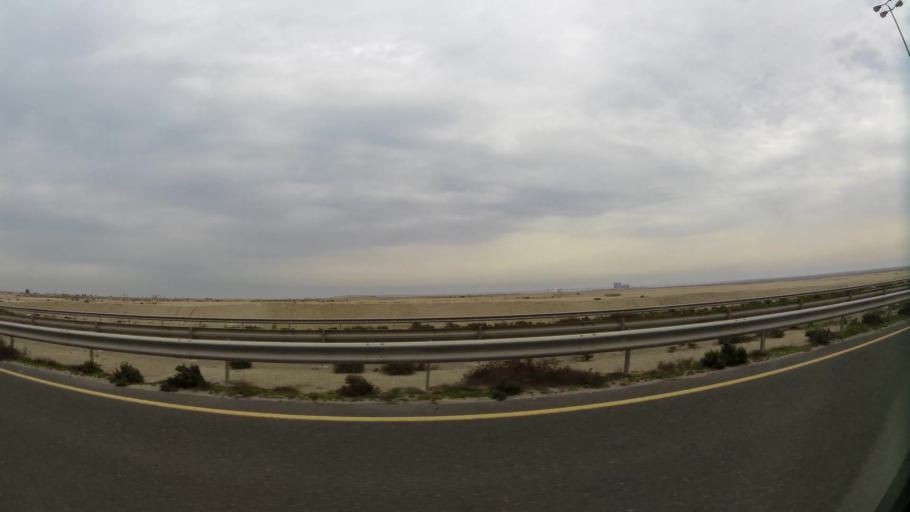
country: BH
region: Central Governorate
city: Dar Kulayb
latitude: 25.8789
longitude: 50.5774
